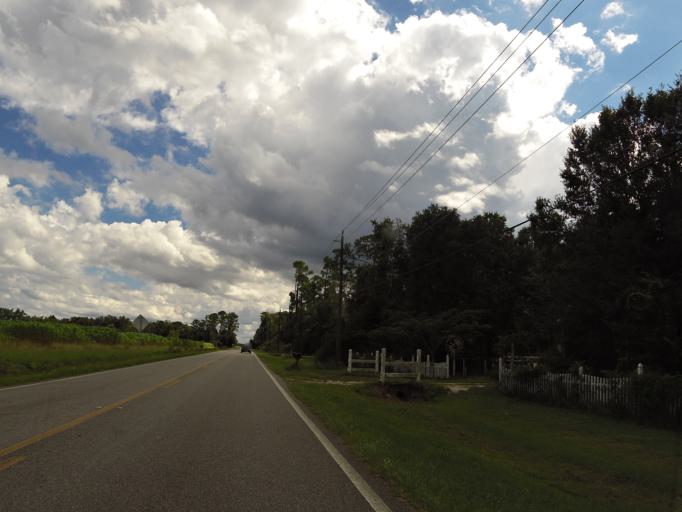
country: US
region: Florida
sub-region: Saint Johns County
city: Saint Augustine South
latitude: 29.8160
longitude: -81.4846
